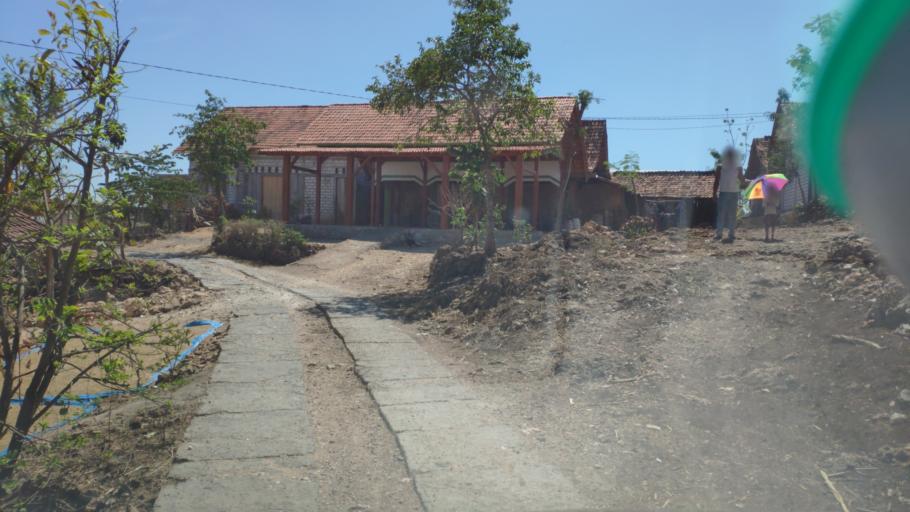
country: ID
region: Central Java
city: Jurangjero
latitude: -6.8942
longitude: 111.5098
